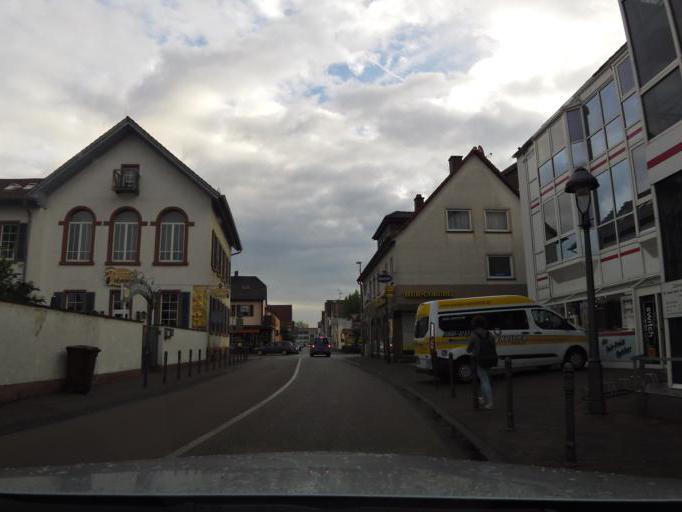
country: DE
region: Hesse
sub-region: Regierungsbezirk Darmstadt
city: Gross-Gerau
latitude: 49.9190
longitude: 8.4860
